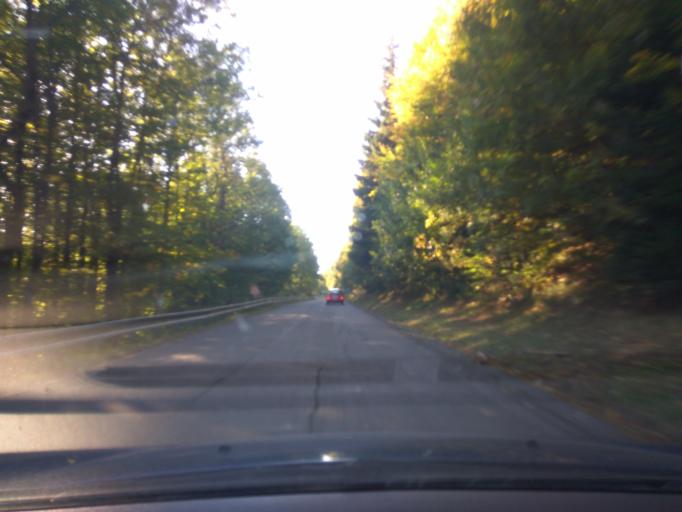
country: SK
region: Banskobystricky
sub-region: Okres Ziar nad Hronom
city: Kremnica
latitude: 48.7352
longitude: 18.9916
